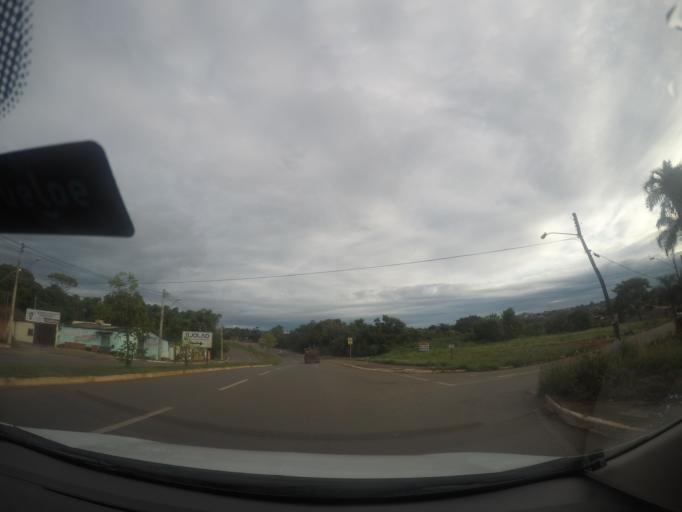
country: BR
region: Goias
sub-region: Goiania
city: Goiania
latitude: -16.6186
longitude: -49.3387
